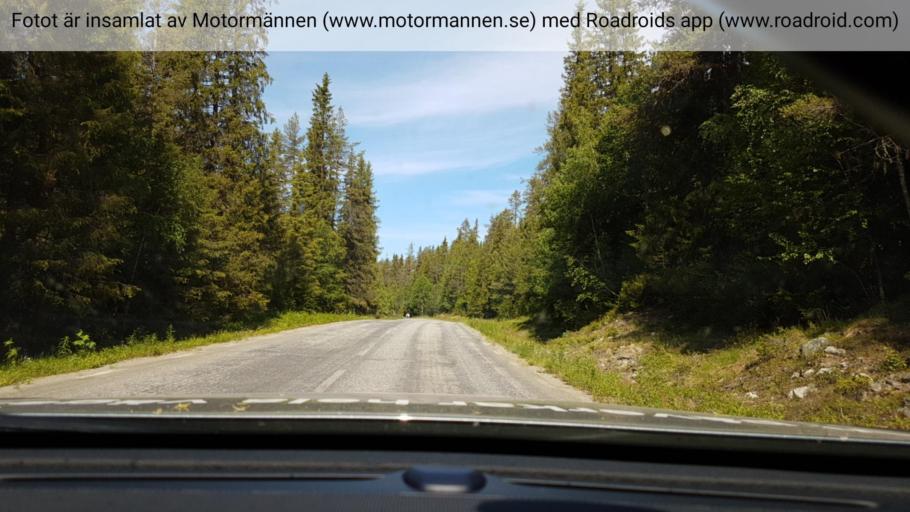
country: SE
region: Vaesterbotten
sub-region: Vilhelmina Kommun
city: Sjoberg
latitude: 64.6250
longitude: 15.8333
